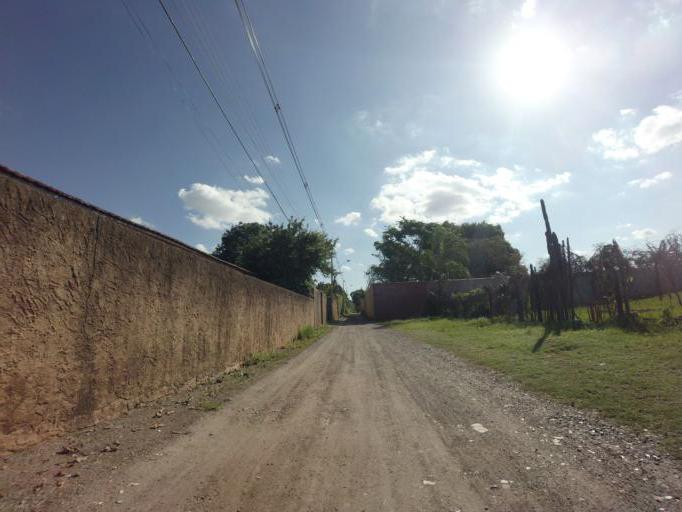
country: BR
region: Sao Paulo
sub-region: Piracicaba
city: Piracicaba
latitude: -22.7340
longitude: -47.5980
